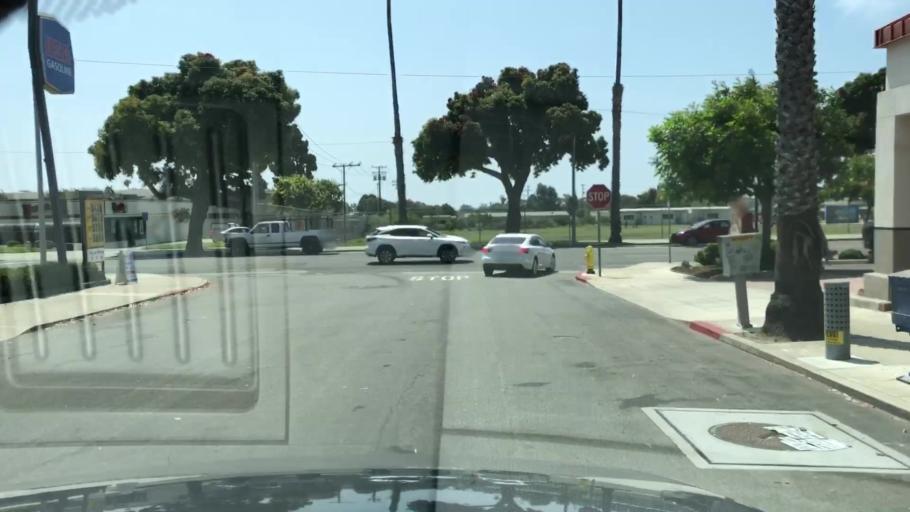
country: US
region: California
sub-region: Ventura County
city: Ventura
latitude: 34.2730
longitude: -119.2612
